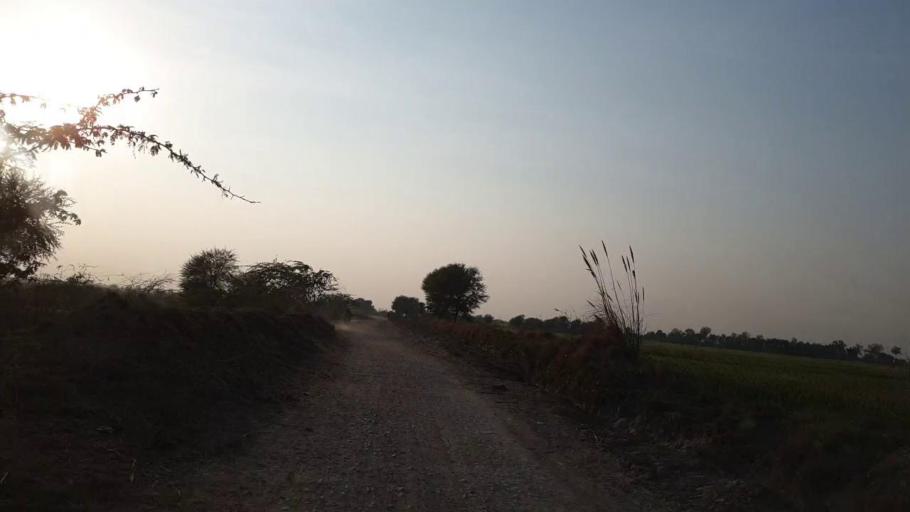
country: PK
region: Sindh
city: Pithoro
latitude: 25.6543
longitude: 69.2231
